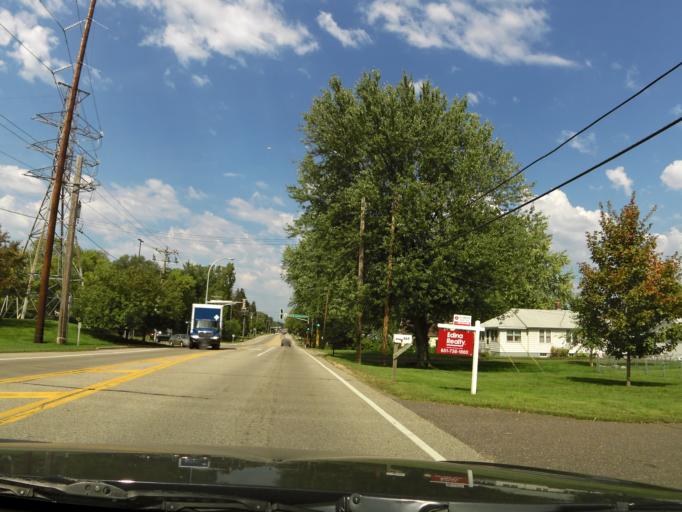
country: US
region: Minnesota
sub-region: Ramsey County
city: Maplewood
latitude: 44.9550
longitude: -92.9846
